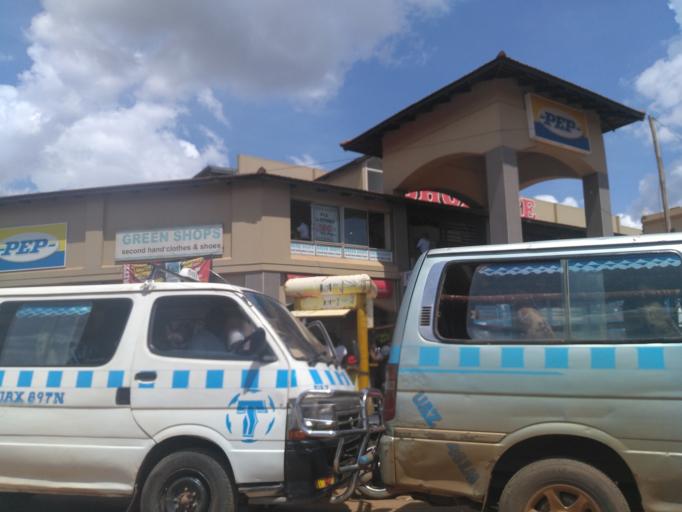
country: UG
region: Central Region
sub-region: Kampala District
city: Kampala
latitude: 0.3094
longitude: 32.5775
